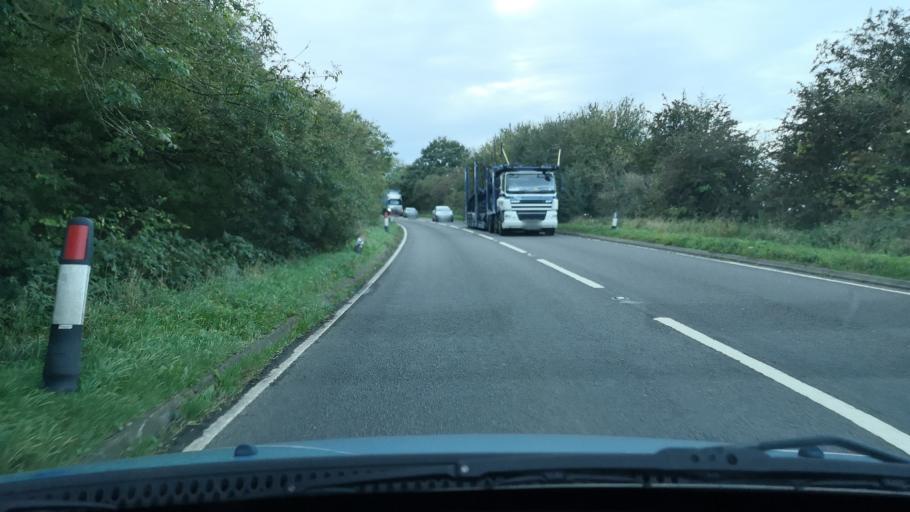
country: GB
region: England
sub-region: North Lincolnshire
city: Crowle
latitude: 53.5879
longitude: -0.8288
